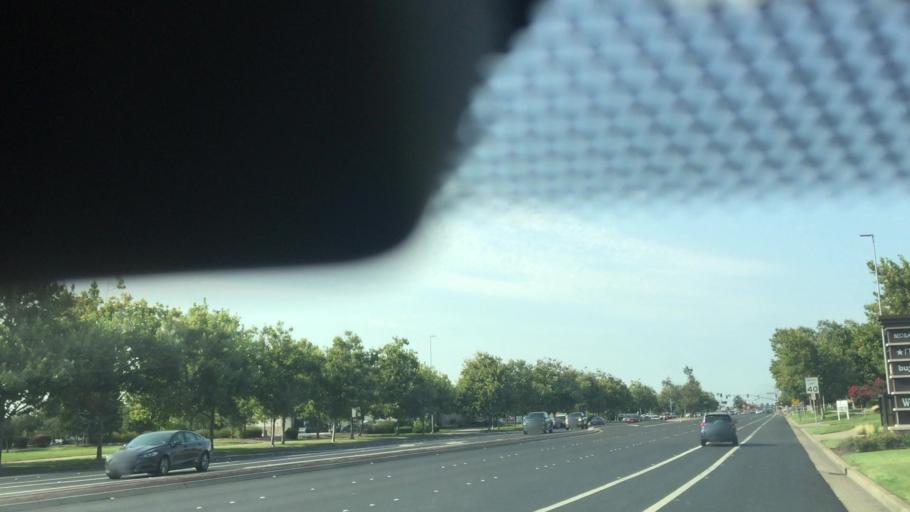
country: US
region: California
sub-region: Placer County
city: Roseville
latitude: 38.7690
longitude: -121.2656
